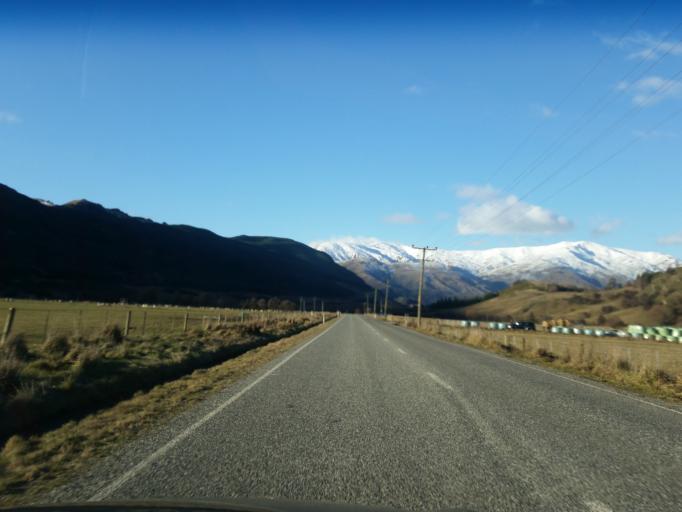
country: NZ
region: Otago
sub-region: Queenstown-Lakes District
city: Arrowtown
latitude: -44.9517
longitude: 168.7517
